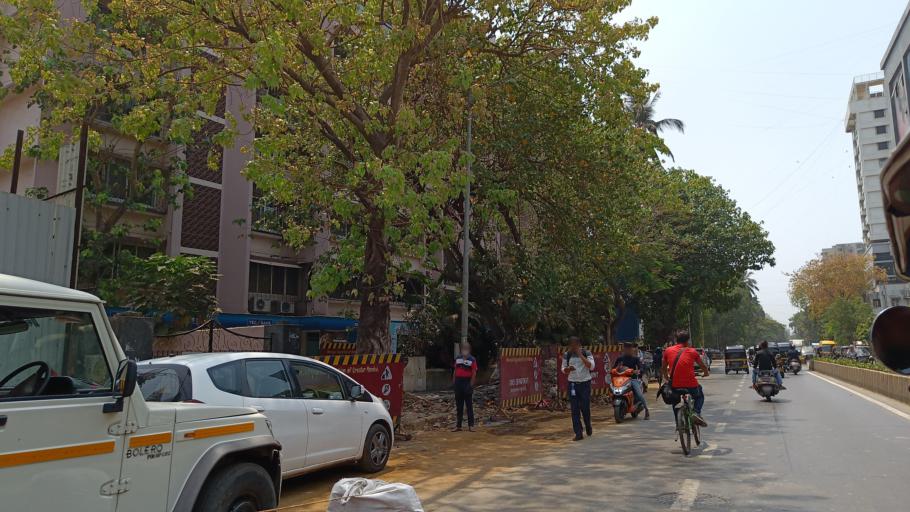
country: IN
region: Maharashtra
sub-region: Mumbai Suburban
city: Mumbai
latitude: 19.0815
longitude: 72.8345
